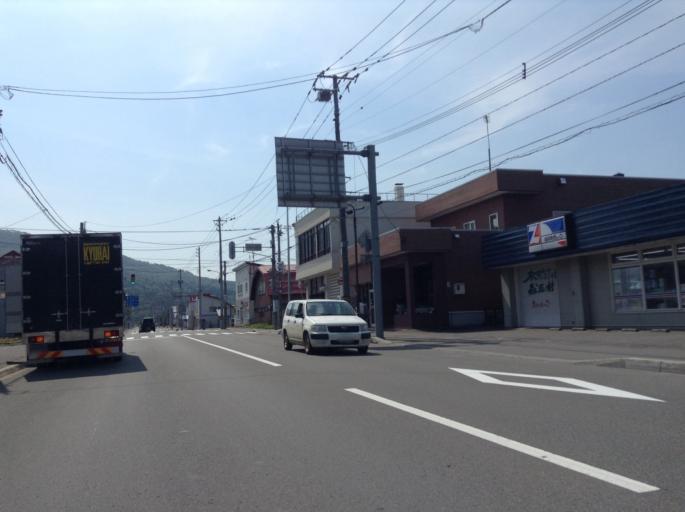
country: JP
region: Hokkaido
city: Nayoro
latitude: 44.7283
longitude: 142.2580
